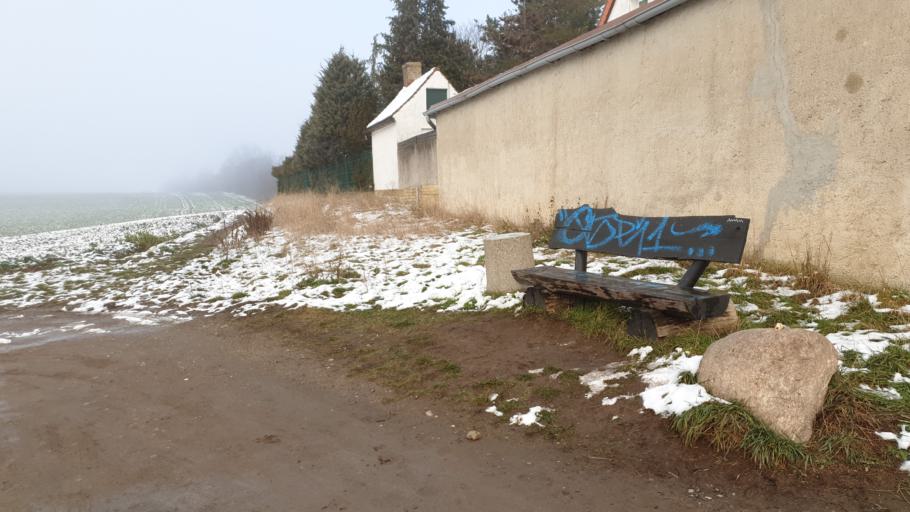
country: DE
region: Saxony
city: Taucha
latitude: 51.3954
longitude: 12.4760
